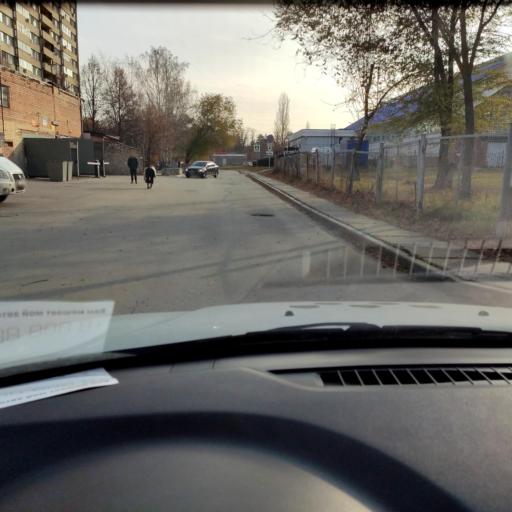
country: RU
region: Samara
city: Tol'yatti
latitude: 53.5047
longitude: 49.4274
